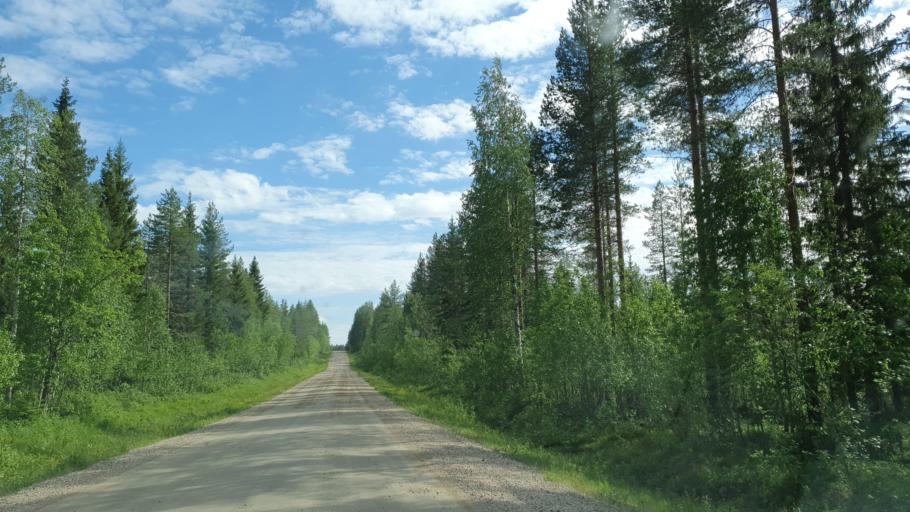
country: FI
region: Kainuu
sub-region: Kehys-Kainuu
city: Kuhmo
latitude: 64.4999
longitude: 29.4892
